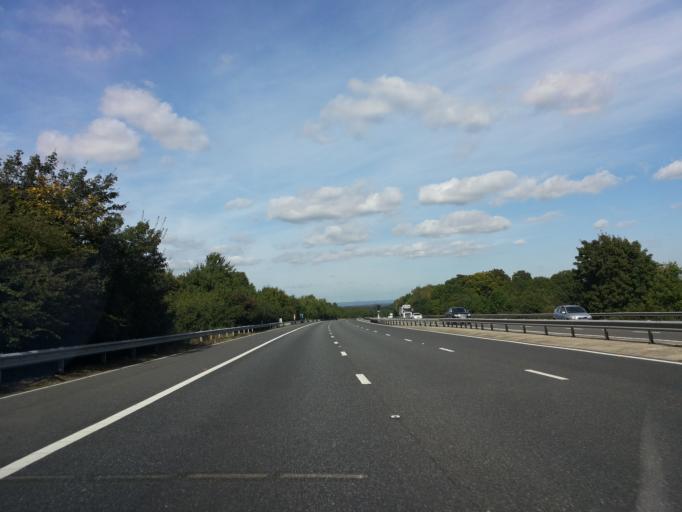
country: GB
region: England
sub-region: Kent
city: Borough Green
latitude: 51.3314
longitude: 0.2732
